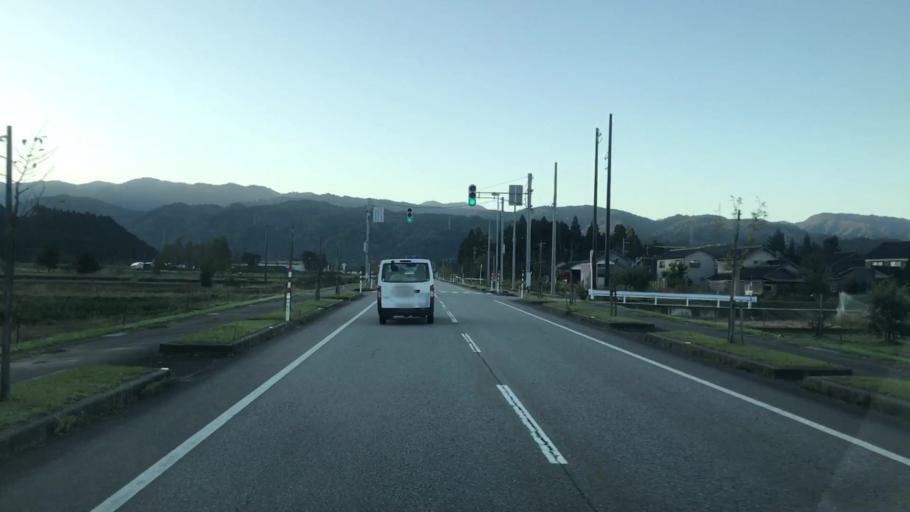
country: JP
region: Toyama
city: Kamiichi
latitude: 36.5982
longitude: 137.3269
